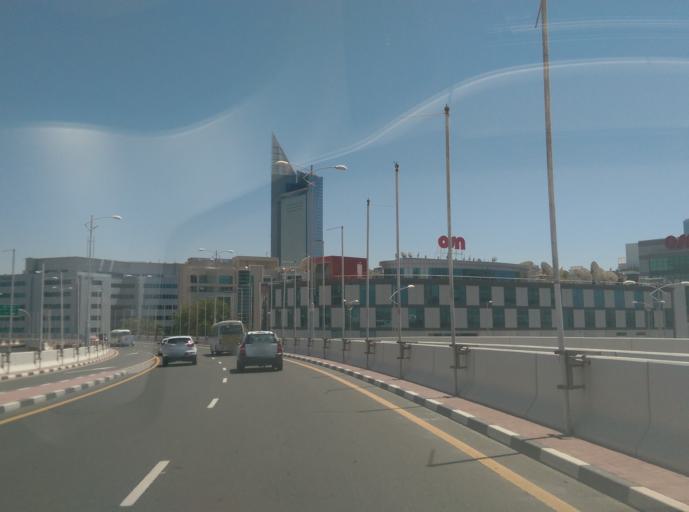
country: AE
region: Dubai
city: Dubai
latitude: 25.0984
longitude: 55.1577
